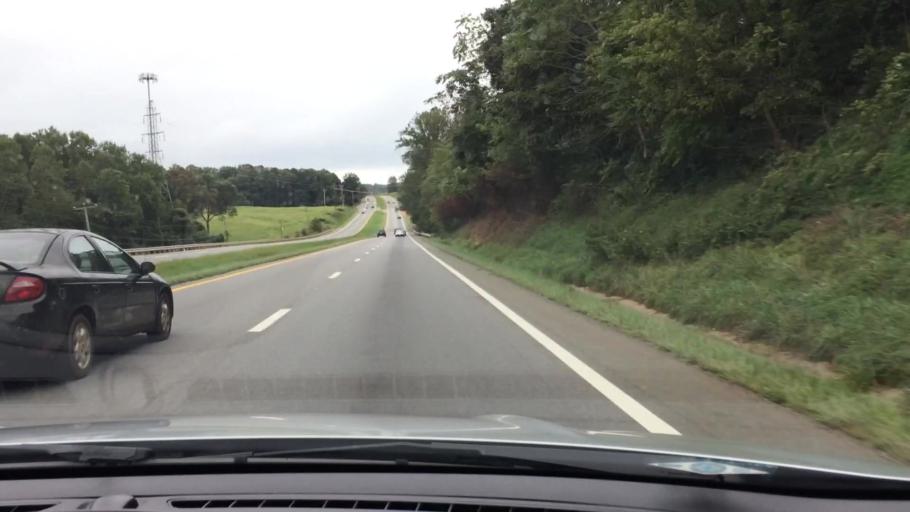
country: US
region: Virginia
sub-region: Franklin County
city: Rocky Mount
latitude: 37.0827
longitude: -79.9251
